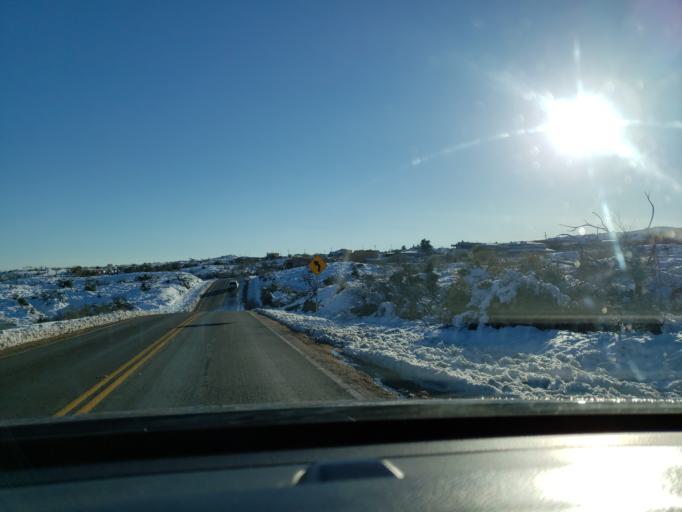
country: US
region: Arizona
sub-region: Maricopa County
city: Carefree
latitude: 33.8721
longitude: -111.8229
